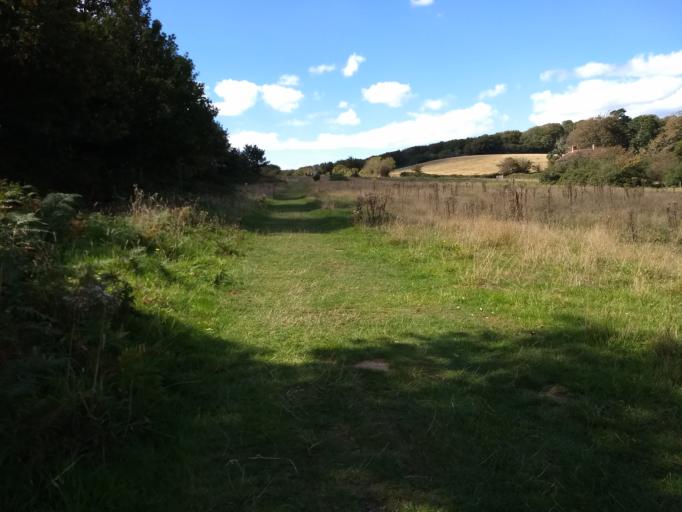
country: GB
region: England
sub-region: Isle of Wight
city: Shalfleet
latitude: 50.6559
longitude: -1.4231
